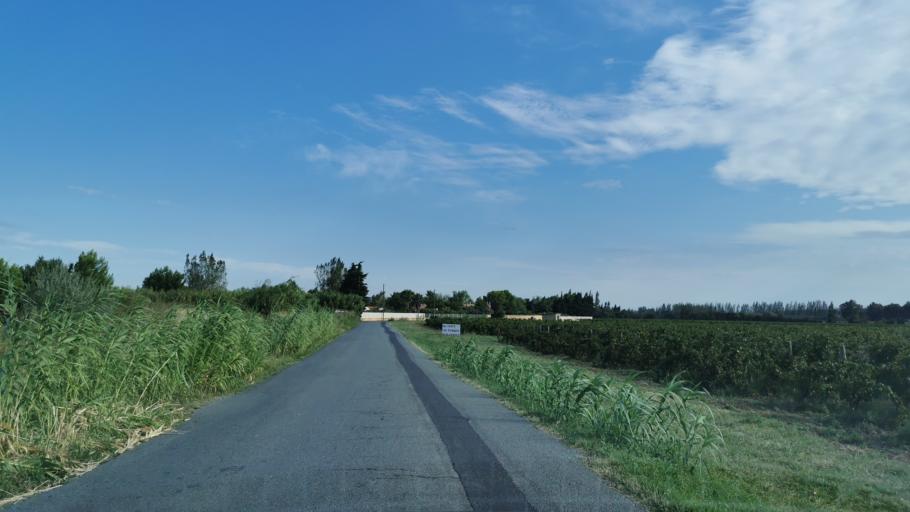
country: FR
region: Languedoc-Roussillon
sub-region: Departement de l'Aude
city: Narbonne
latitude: 43.1343
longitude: 3.0252
